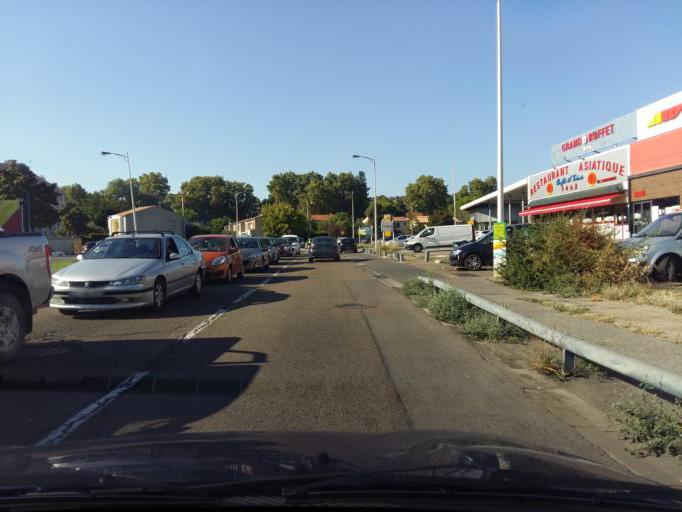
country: FR
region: Languedoc-Roussillon
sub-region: Departement du Gard
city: Nimes
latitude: 43.8190
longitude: 4.3465
